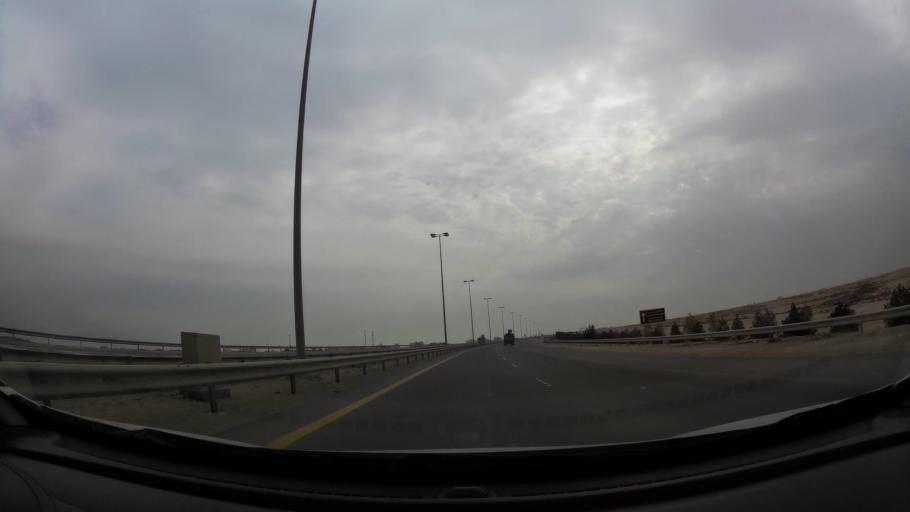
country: BH
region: Northern
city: Ar Rifa'
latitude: 26.0682
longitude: 50.6145
